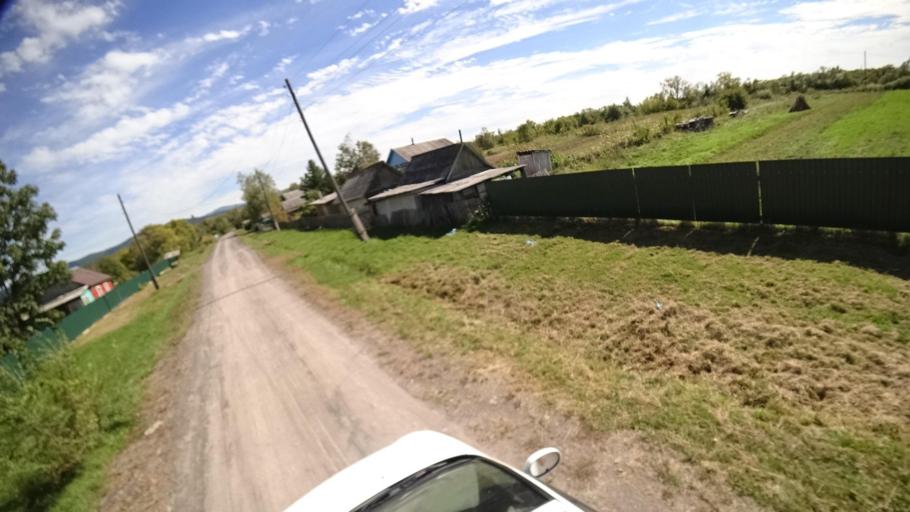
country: RU
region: Primorskiy
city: Yakovlevka
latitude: 44.4314
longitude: 133.5715
